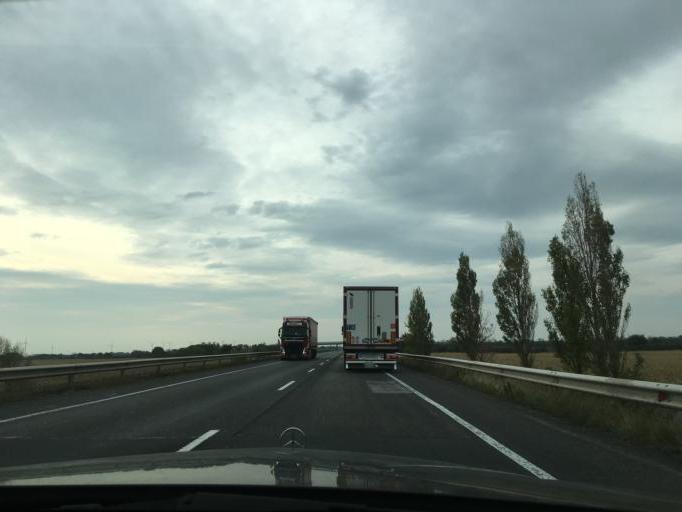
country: HU
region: Gyor-Moson-Sopron
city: Rajka
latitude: 47.9272
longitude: 17.1727
